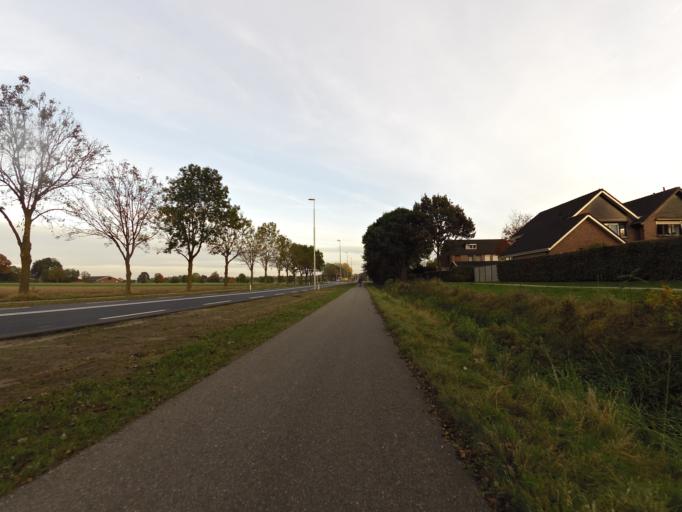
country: NL
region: Gelderland
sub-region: Gemeente Doetinchem
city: Doetinchem
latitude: 51.9652
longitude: 6.2157
